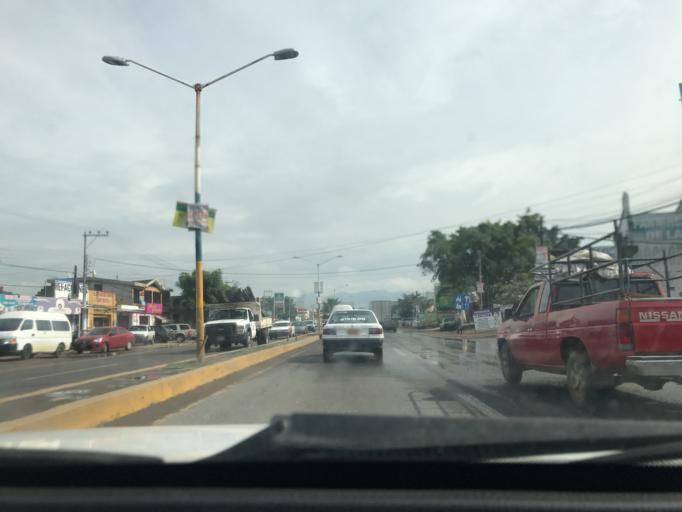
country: MX
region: Morelos
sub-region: Cuautla
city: Tierra Larga (Campo Nuevo)
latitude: 18.8537
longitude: -98.9363
